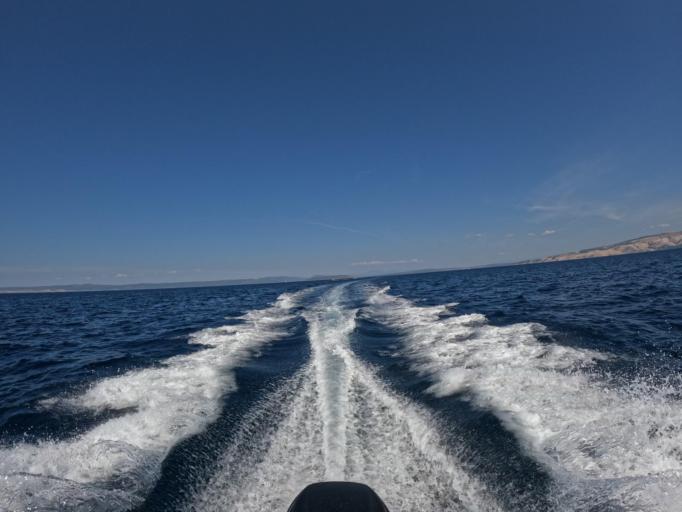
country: HR
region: Primorsko-Goranska
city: Lopar
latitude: 44.8883
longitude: 14.6474
